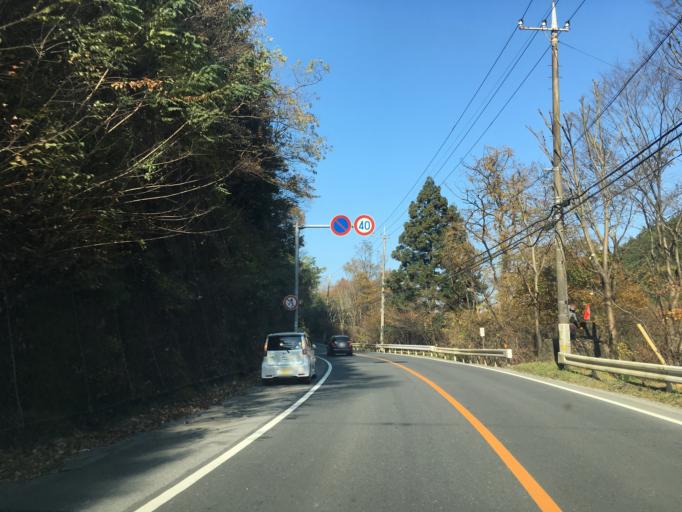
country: JP
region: Saitama
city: Chichibu
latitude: 35.9748
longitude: 139.1155
